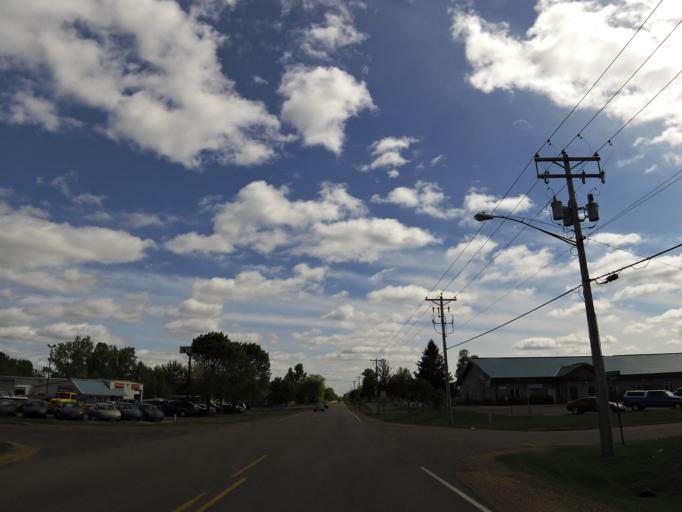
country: US
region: Wisconsin
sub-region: Saint Croix County
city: Hudson
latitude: 44.9605
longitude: -92.7312
